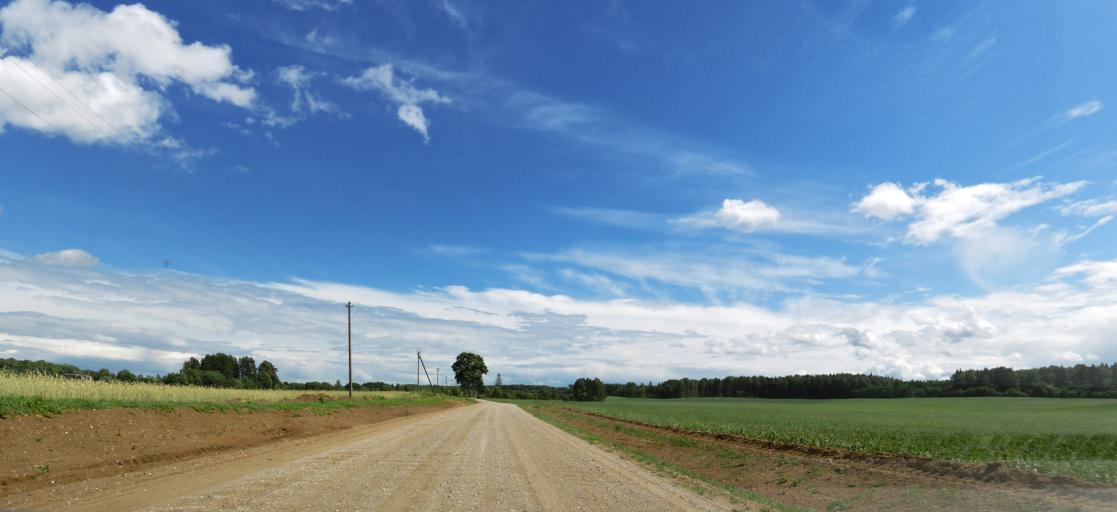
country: LT
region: Panevezys
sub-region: Birzai
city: Birzai
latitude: 56.4123
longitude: 24.8126
